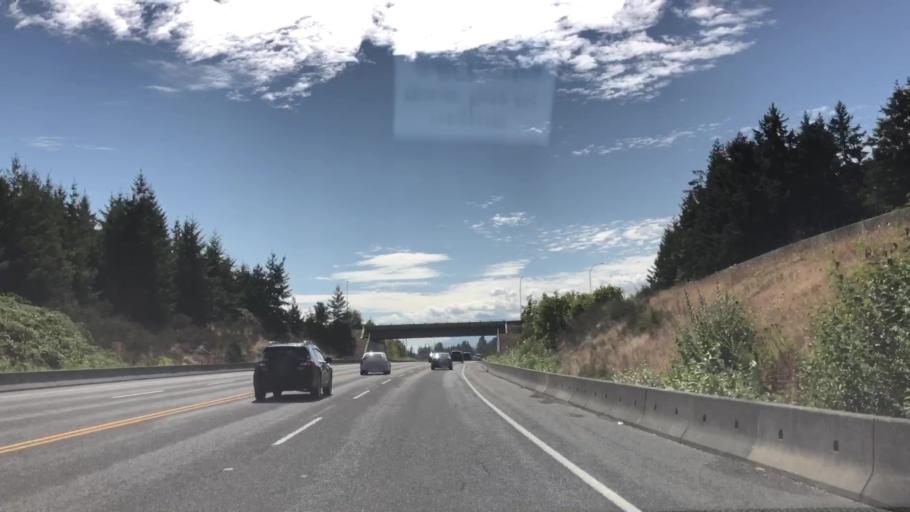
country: CA
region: British Columbia
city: Nanaimo
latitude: 49.1273
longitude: -123.8639
